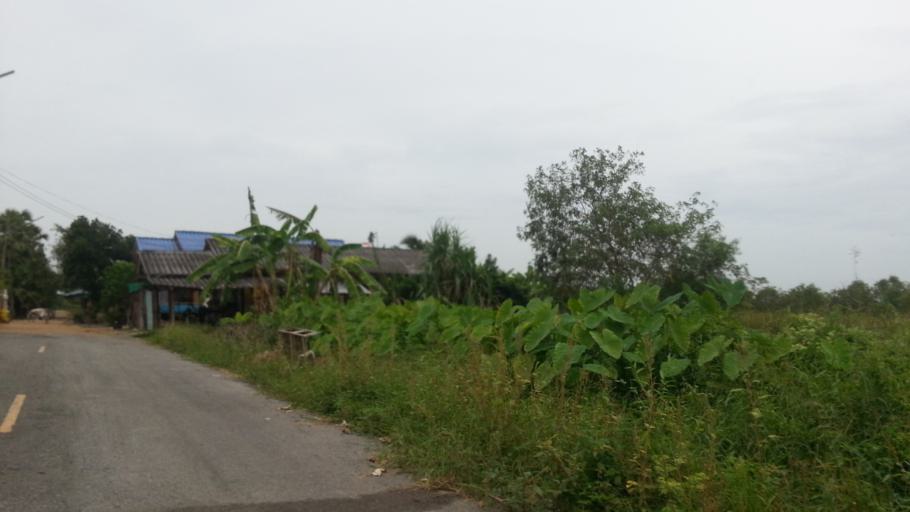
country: TH
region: Pathum Thani
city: Nong Suea
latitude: 14.0632
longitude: 100.8436
